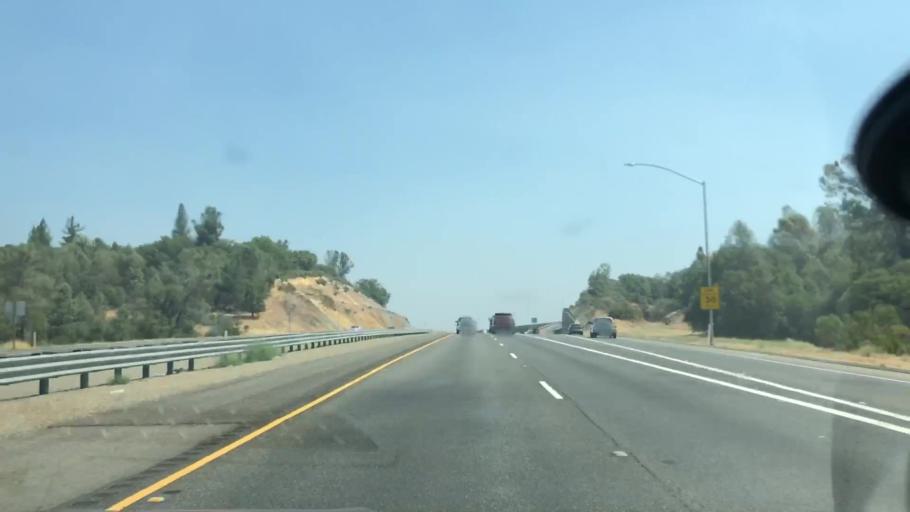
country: US
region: California
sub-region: El Dorado County
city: Shingle Springs
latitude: 38.6872
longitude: -120.9079
